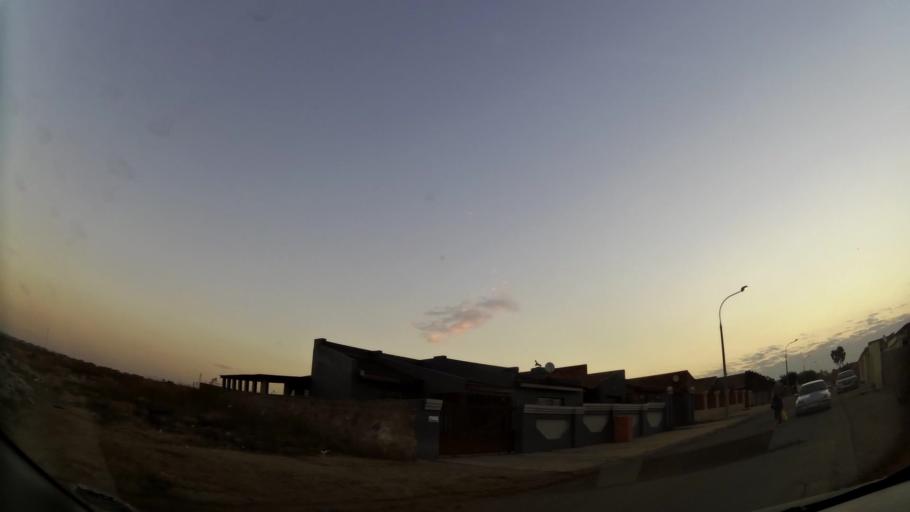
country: ZA
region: Gauteng
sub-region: West Rand District Municipality
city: Randfontein
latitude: -26.2132
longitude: 27.7136
